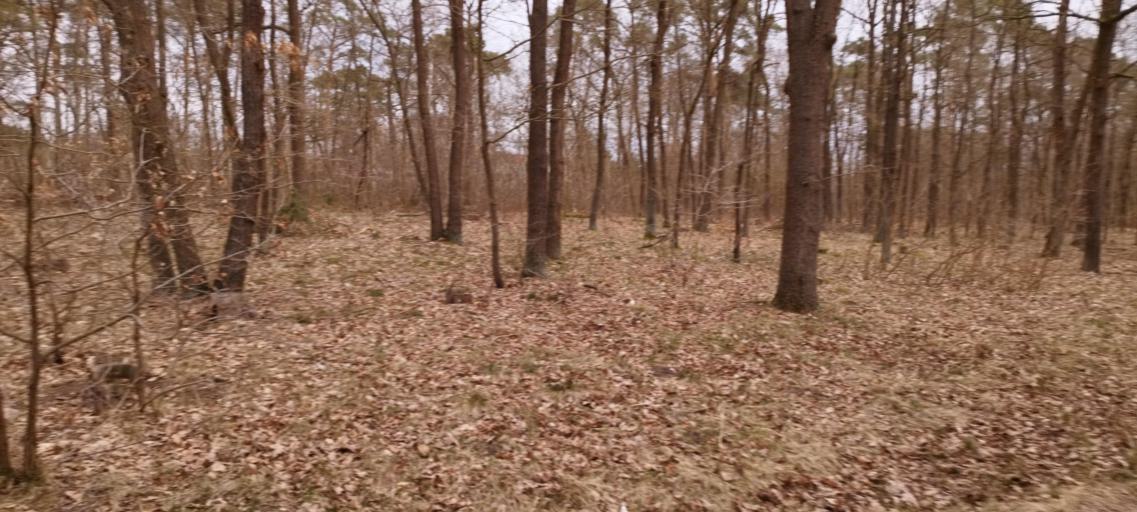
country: DE
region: Brandenburg
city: Grunheide
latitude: 52.4140
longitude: 13.8006
